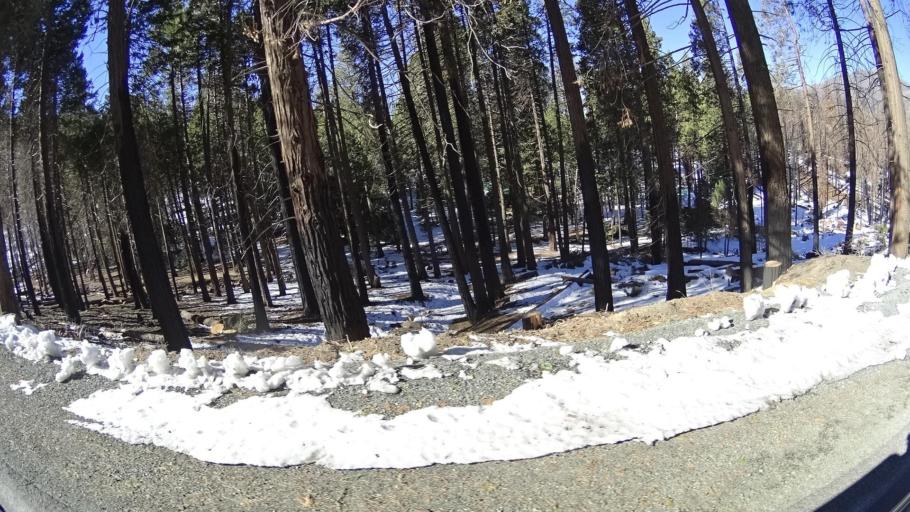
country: US
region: California
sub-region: Kern County
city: Alta Sierra
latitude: 35.7416
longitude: -118.5570
